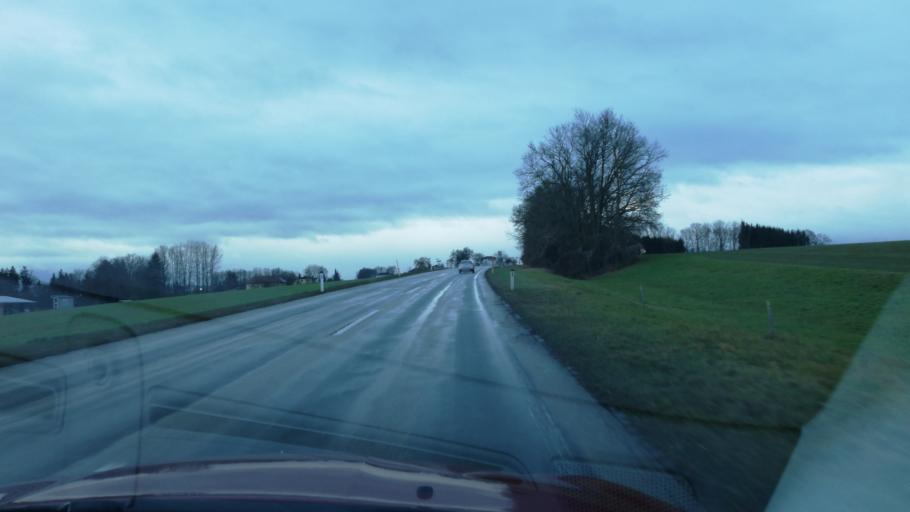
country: AT
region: Upper Austria
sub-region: Wels-Land
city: Sattledt
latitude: 48.0222
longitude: 14.0601
